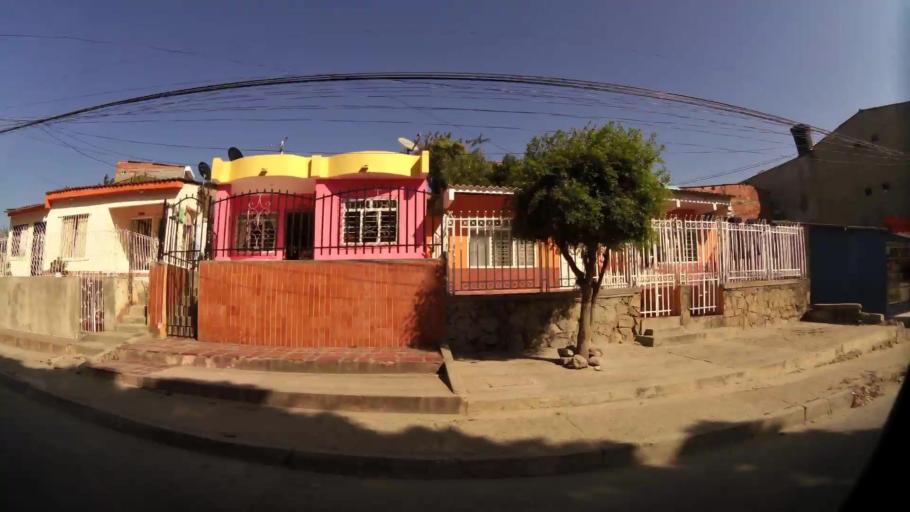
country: CO
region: Bolivar
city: Cartagena
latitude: 10.4263
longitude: -75.5201
